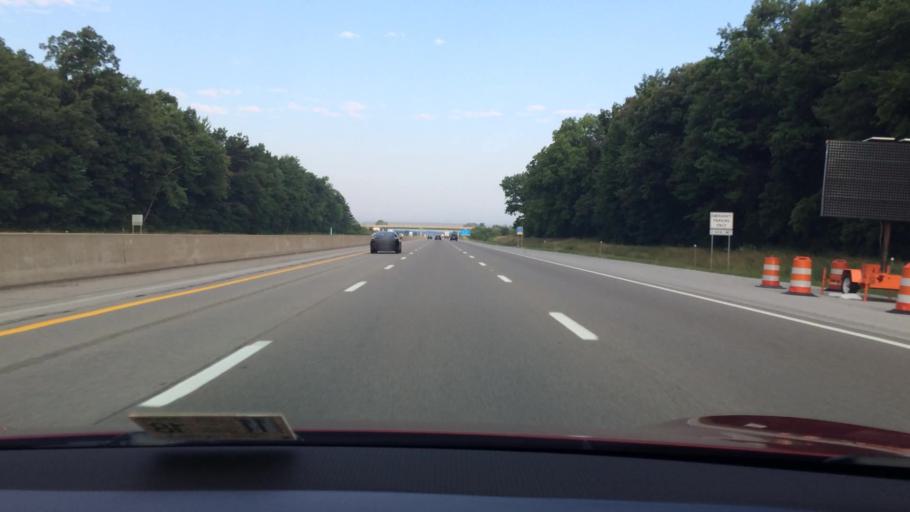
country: US
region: Ohio
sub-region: Sandusky County
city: Clyde
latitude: 41.3597
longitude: -82.9105
